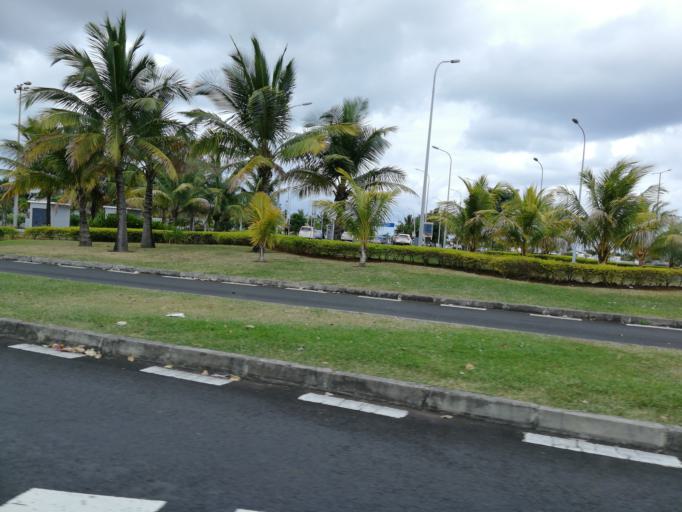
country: MU
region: Grand Port
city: Plaine Magnien
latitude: -20.4333
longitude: 57.6748
